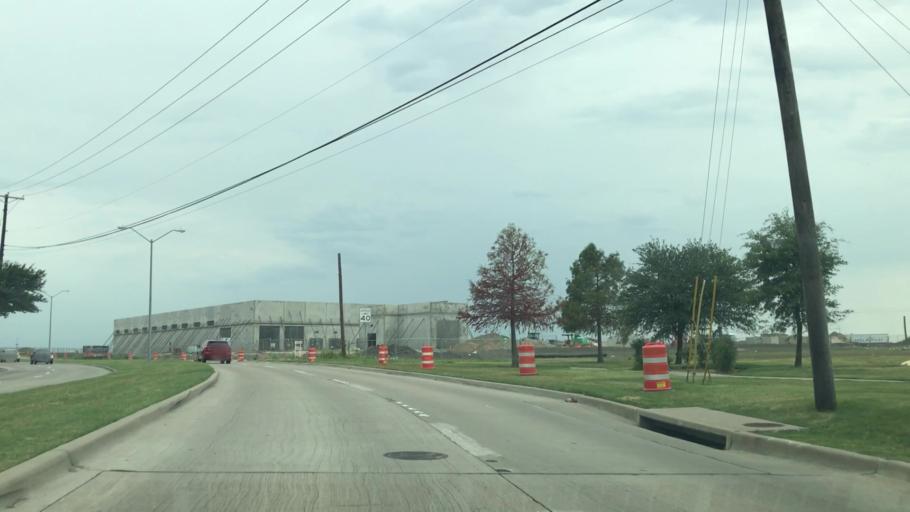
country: US
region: Texas
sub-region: Dallas County
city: Richardson
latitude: 32.9974
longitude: -96.7559
